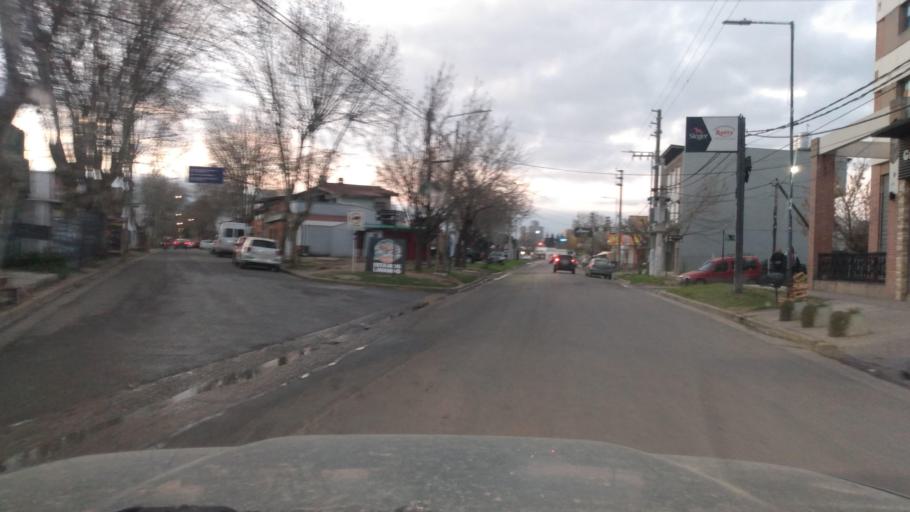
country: AR
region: Buenos Aires
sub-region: Partido de Pilar
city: Pilar
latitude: -34.4651
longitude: -58.9143
